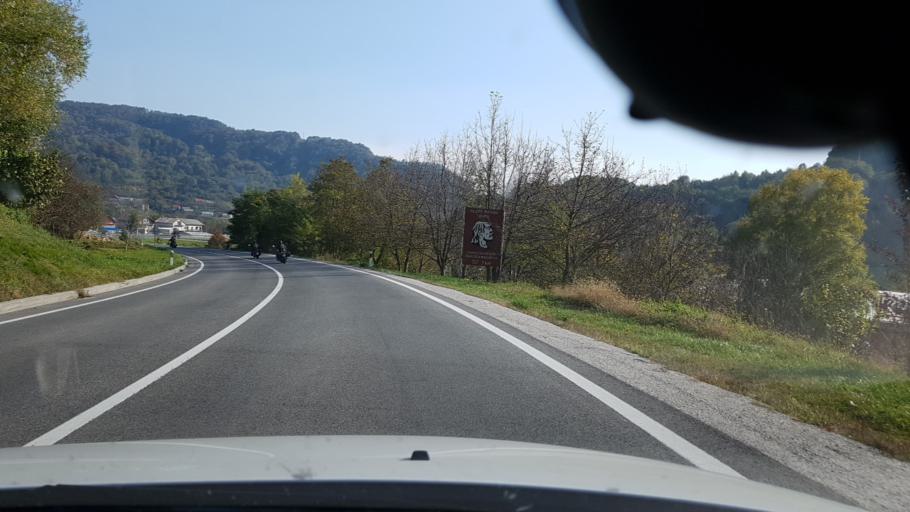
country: HR
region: Krapinsko-Zagorska
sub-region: Grad Krapina
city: Krapina
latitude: 46.1819
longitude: 15.8585
